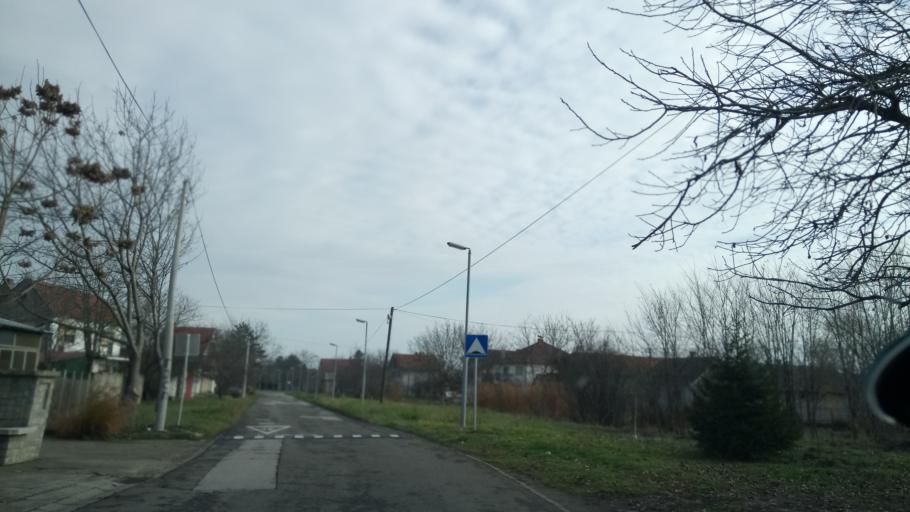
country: RS
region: Autonomna Pokrajina Vojvodina
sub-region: Sremski Okrug
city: Stara Pazova
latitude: 44.9772
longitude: 20.1591
